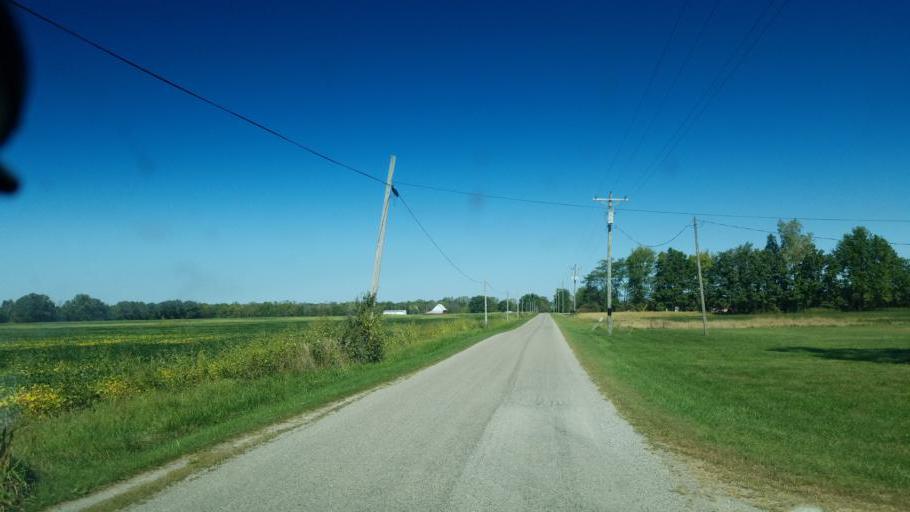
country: US
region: Ohio
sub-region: Union County
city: Richwood
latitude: 40.4693
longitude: -83.4051
